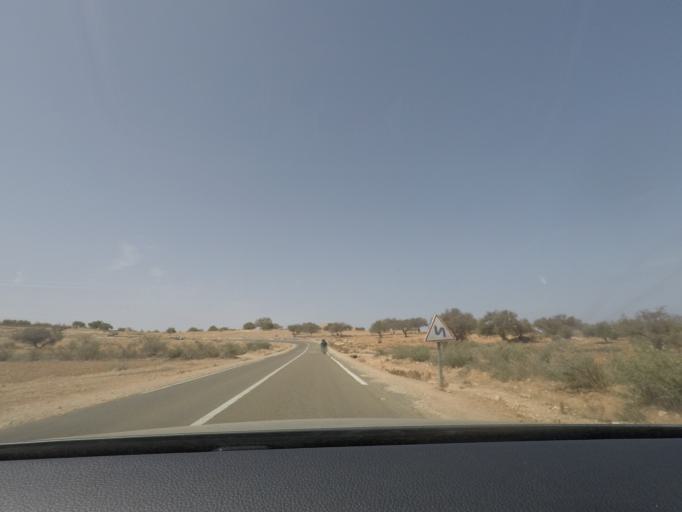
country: MA
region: Marrakech-Tensift-Al Haouz
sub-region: Essaouira
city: Tamanar
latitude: 31.0353
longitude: -9.6724
